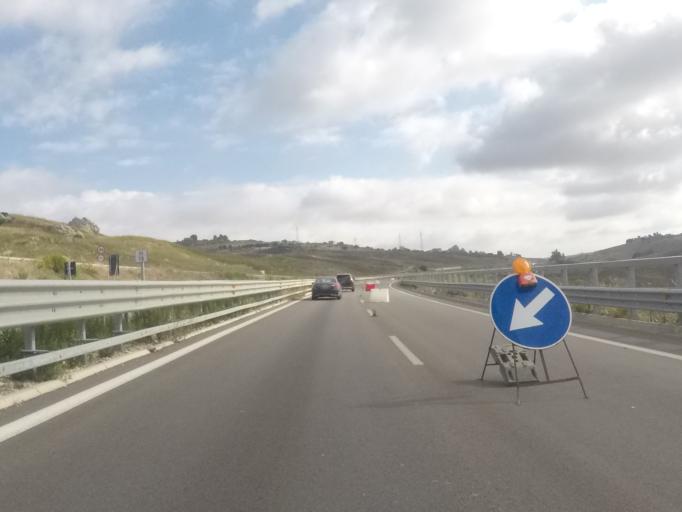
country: IT
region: Sicily
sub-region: Agrigento
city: Agrigento
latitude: 37.3371
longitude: 13.6226
